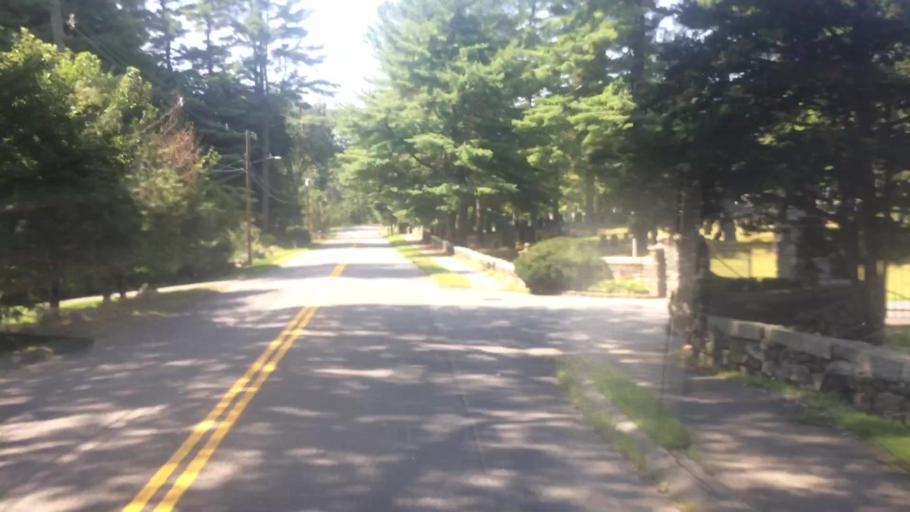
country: US
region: Massachusetts
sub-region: Middlesex County
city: Acton
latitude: 42.4786
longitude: -71.4226
